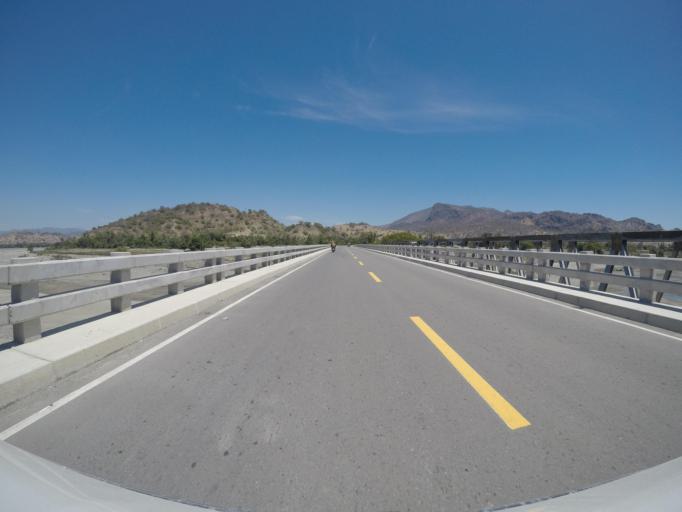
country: TL
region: Manatuto
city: Manatuto
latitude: -8.5179
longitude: 126.0015
